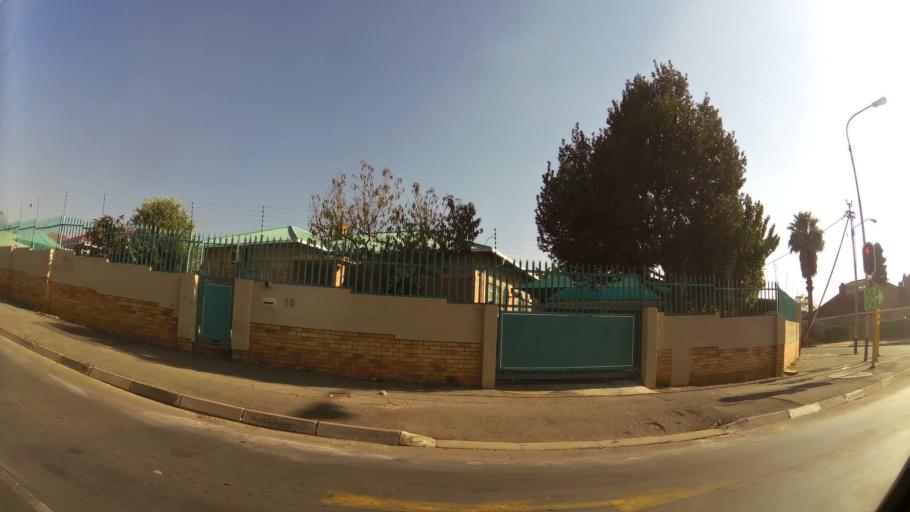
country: ZA
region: Gauteng
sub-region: Ekurhuleni Metropolitan Municipality
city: Germiston
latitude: -26.1979
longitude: 28.1290
